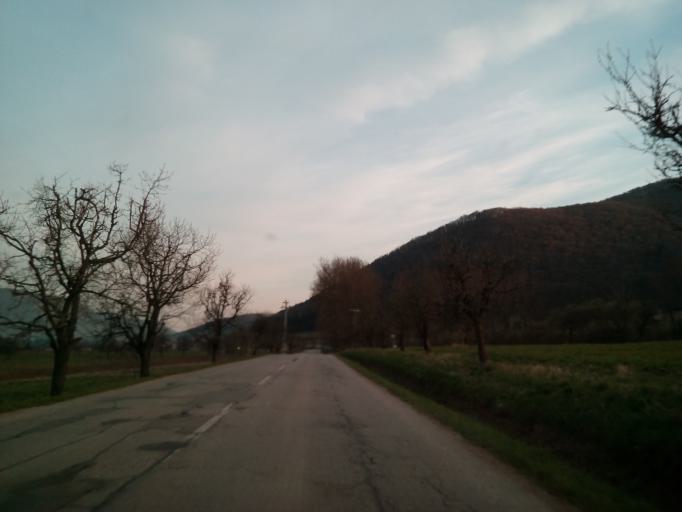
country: SK
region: Kosicky
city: Dobsina
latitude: 48.6716
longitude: 20.3575
